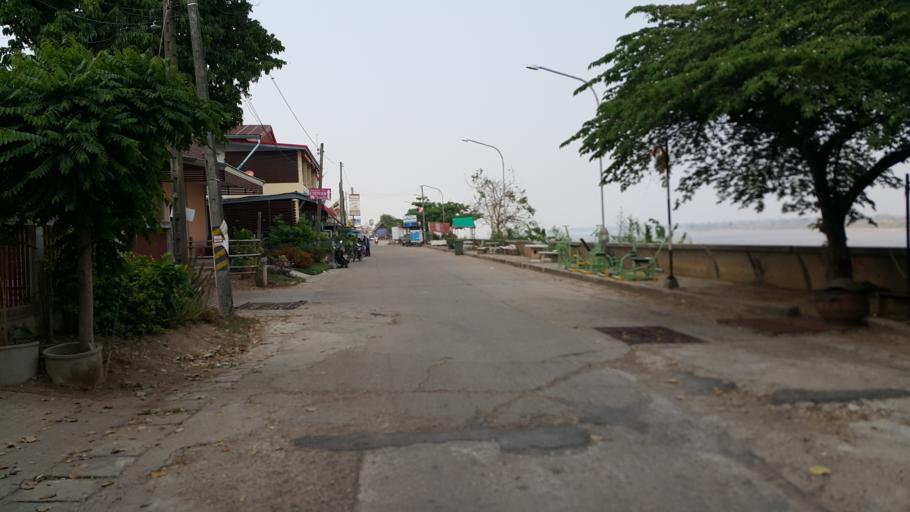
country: TH
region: Nakhon Phanom
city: That Phanom
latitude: 16.9413
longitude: 104.7292
